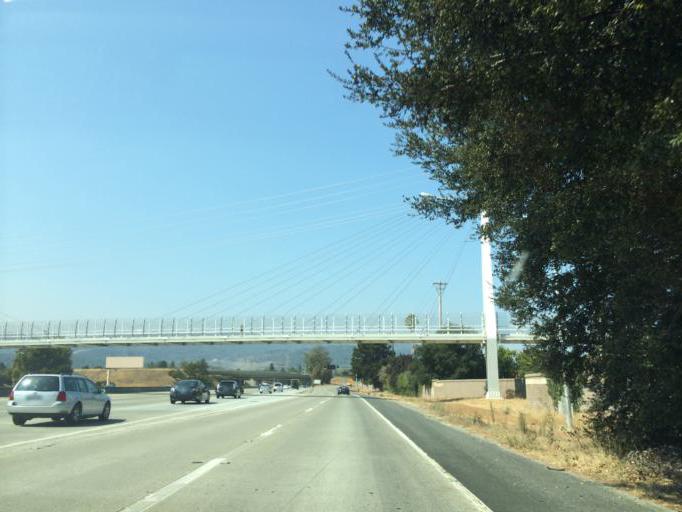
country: US
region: California
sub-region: Santa Clara County
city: Cupertino
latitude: 37.3339
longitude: -122.0498
